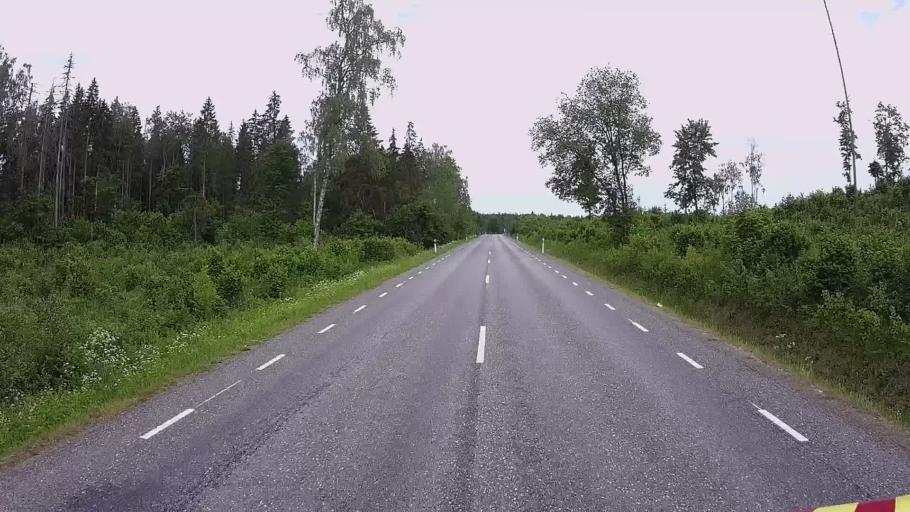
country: EE
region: Laeaene-Virumaa
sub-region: Vaeike-Maarja vald
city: Vaike-Maarja
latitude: 59.0949
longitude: 26.2292
